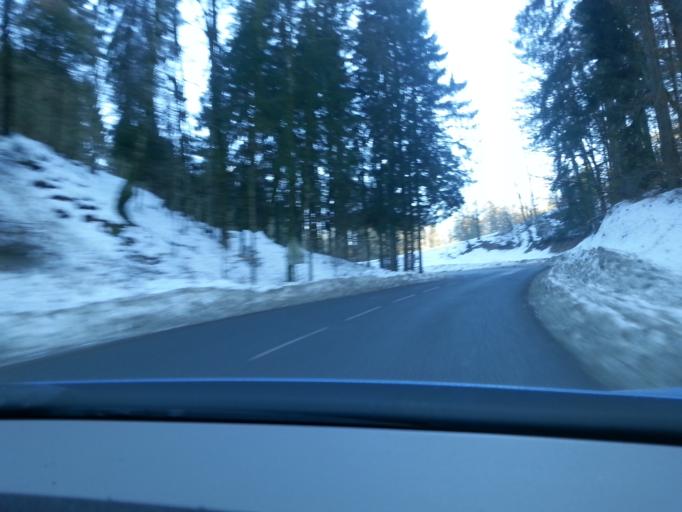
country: FR
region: Rhone-Alpes
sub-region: Departement de la Haute-Savoie
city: Samoens
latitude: 46.0760
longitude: 6.7148
